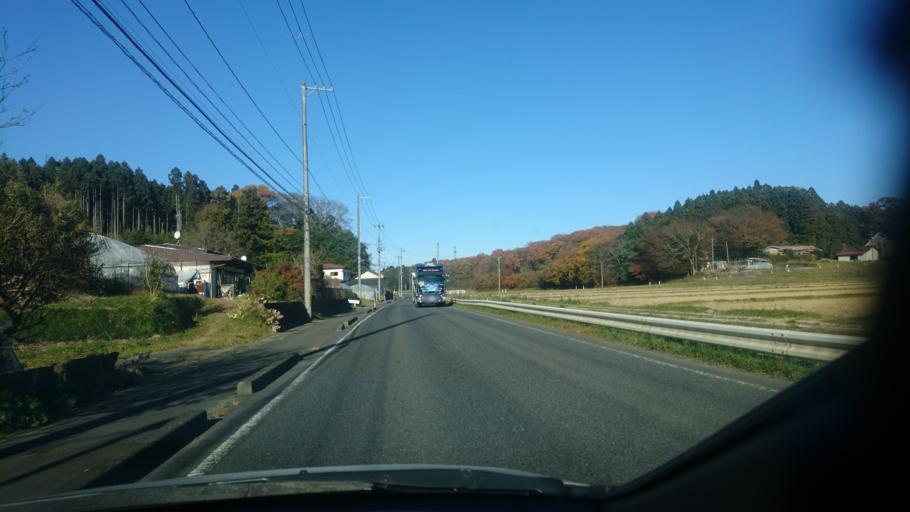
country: JP
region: Miyagi
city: Tomiya
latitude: 38.4571
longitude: 140.9032
